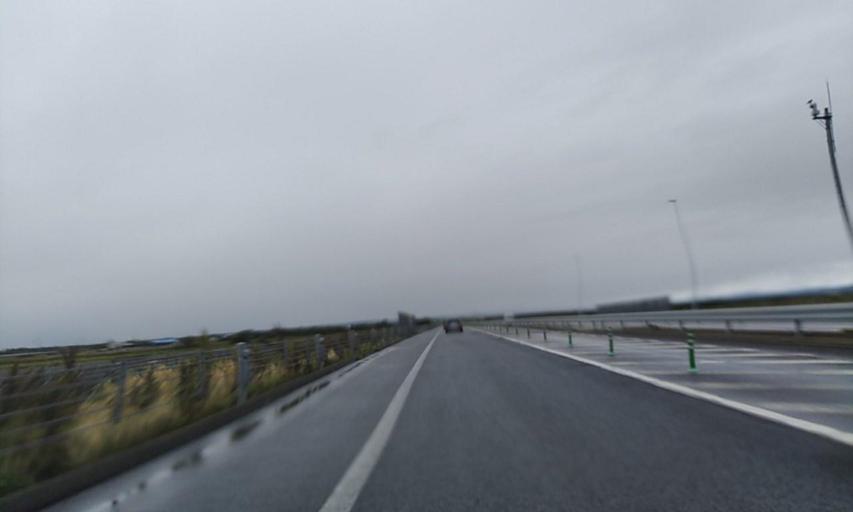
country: JP
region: Hokkaido
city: Kushiro
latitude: 43.0369
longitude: 144.3501
